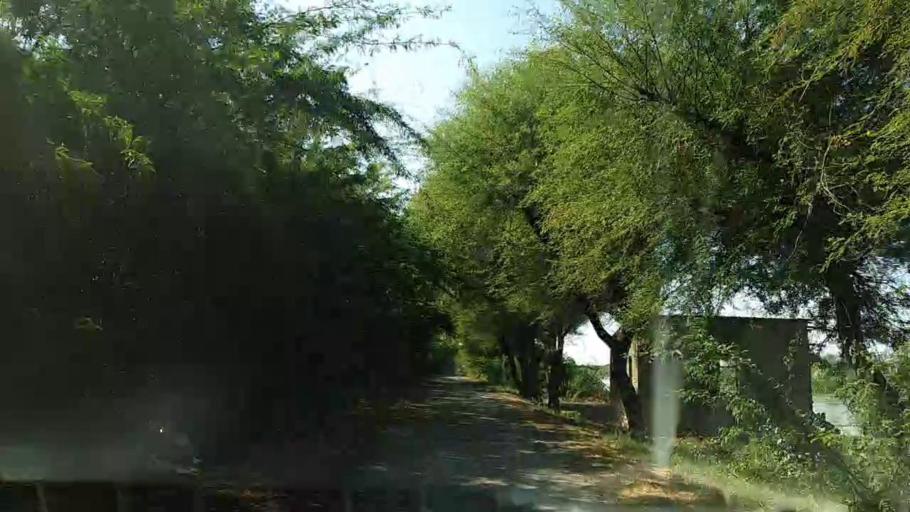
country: PK
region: Sindh
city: Chuhar Jamali
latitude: 24.5747
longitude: 68.0448
